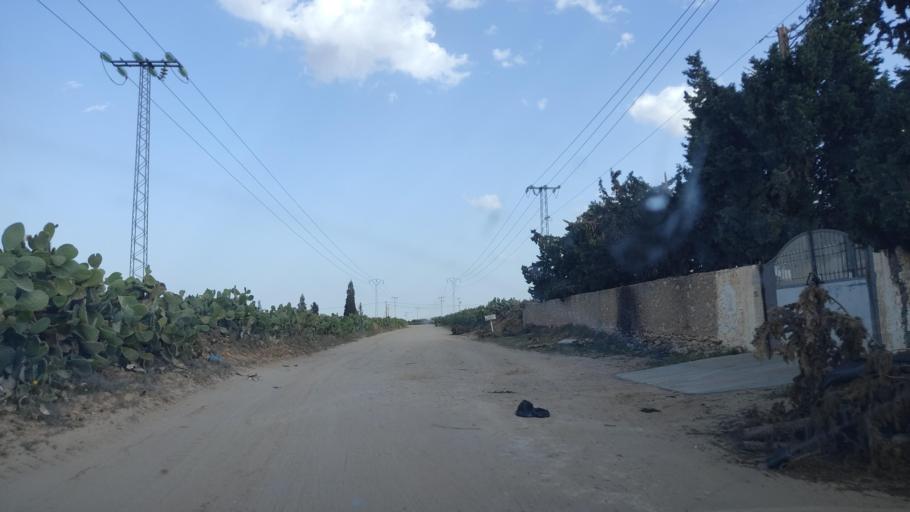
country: TN
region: Safaqis
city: Sfax
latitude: 34.8579
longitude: 10.6035
